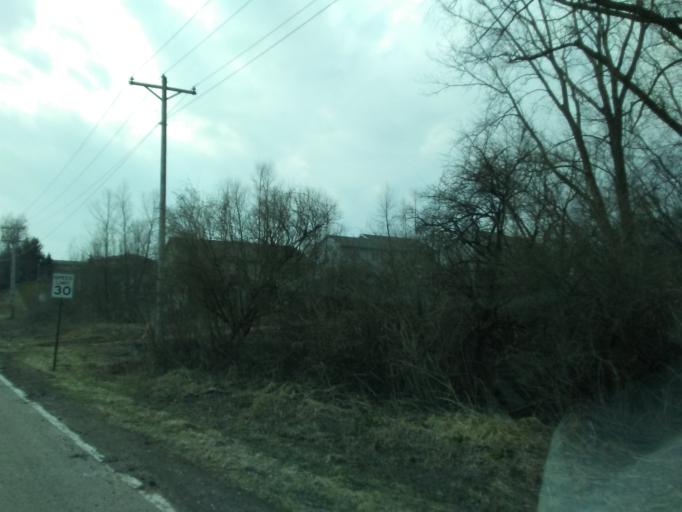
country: US
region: Wisconsin
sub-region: Dane County
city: Middleton
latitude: 43.1178
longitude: -89.4914
